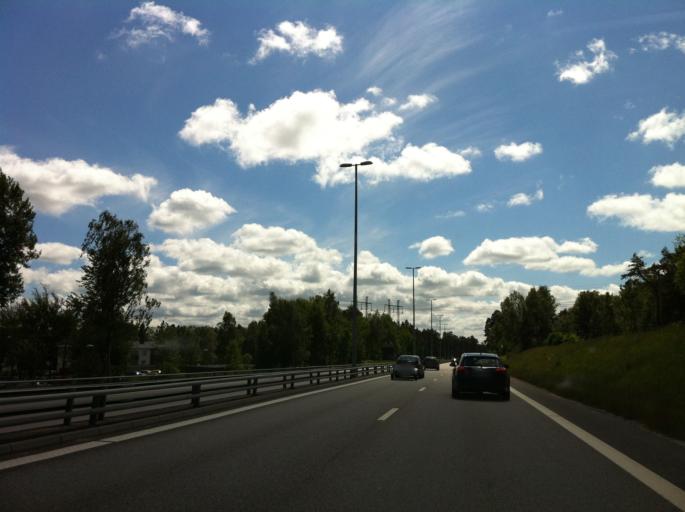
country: SE
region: Vaestra Goetaland
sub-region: Trollhattan
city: Trollhattan
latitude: 58.2688
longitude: 12.2957
